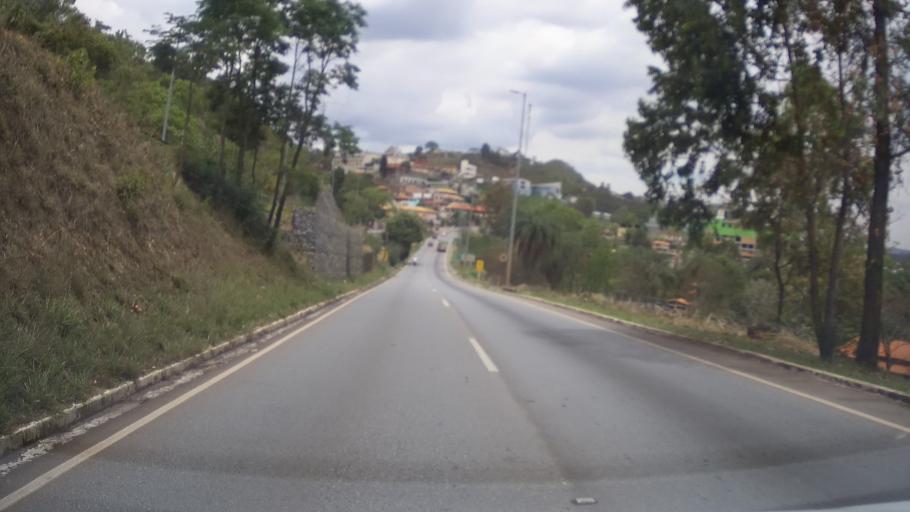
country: BR
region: Minas Gerais
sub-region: Nova Lima
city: Nova Lima
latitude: -19.9986
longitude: -43.8849
